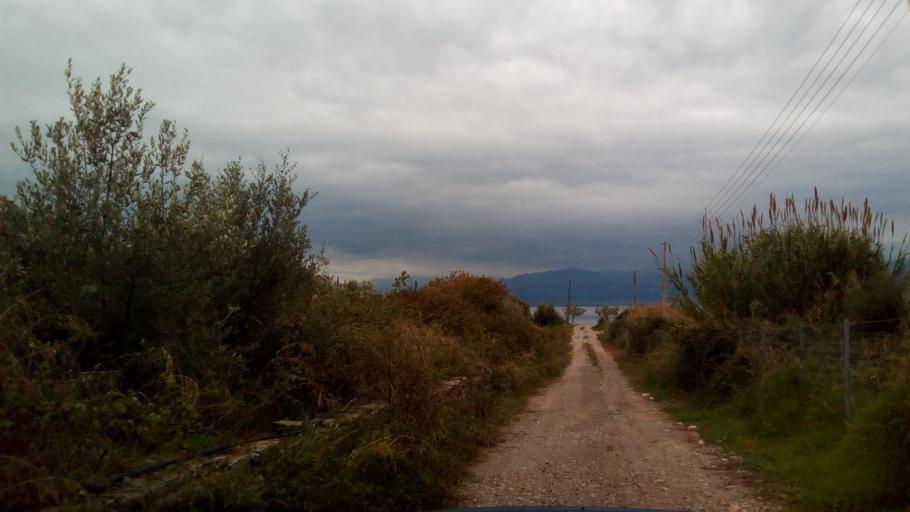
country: GR
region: West Greece
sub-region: Nomos Achaias
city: Kamarai
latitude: 38.3893
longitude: 22.0644
